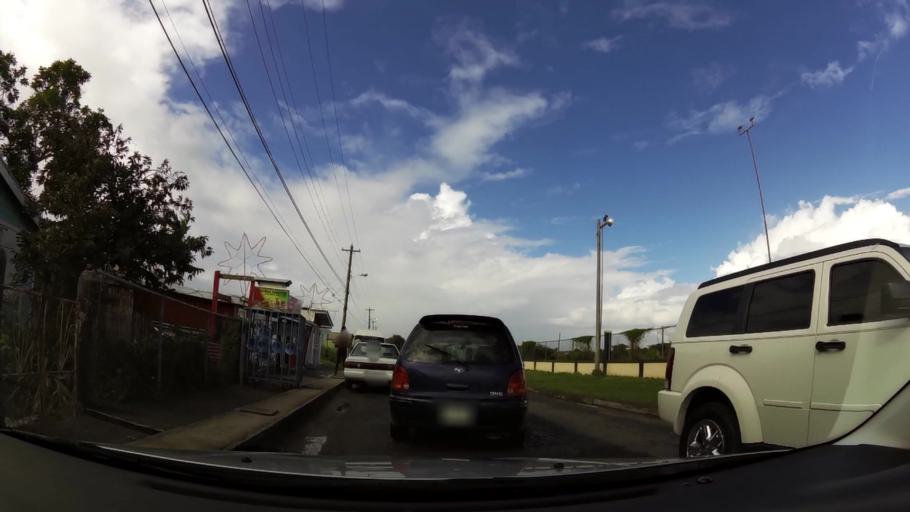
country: AG
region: Saint George
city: Piggotts
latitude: 17.1131
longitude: -61.8176
